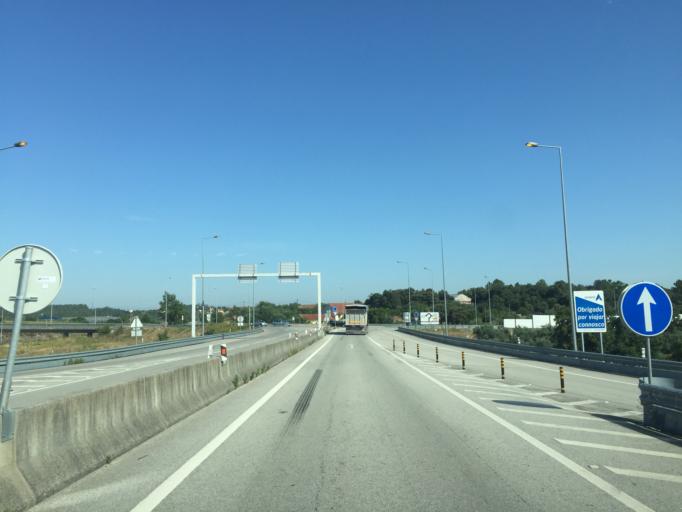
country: PT
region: Santarem
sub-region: Ferreira do Zezere
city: Ferreira do Zezere
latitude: 39.6687
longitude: -8.3587
